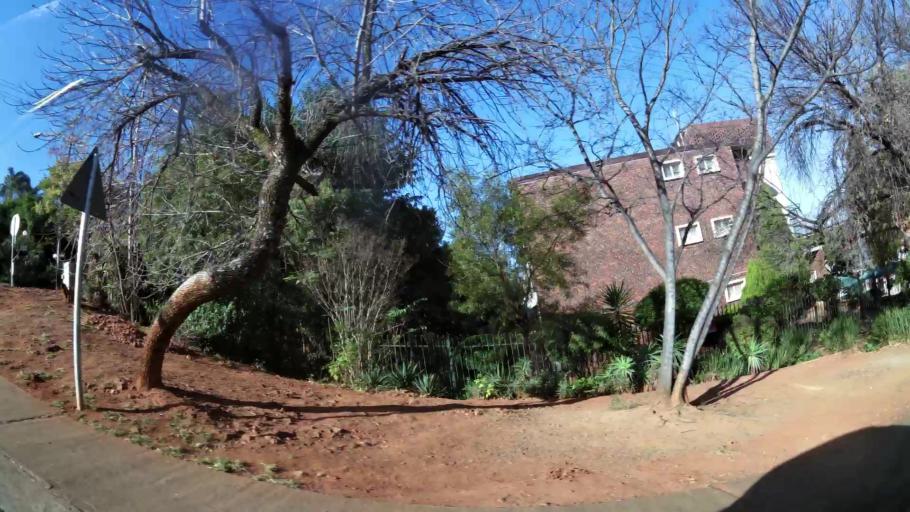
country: ZA
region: Gauteng
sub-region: City of Tshwane Metropolitan Municipality
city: Pretoria
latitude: -25.6955
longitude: 28.2427
